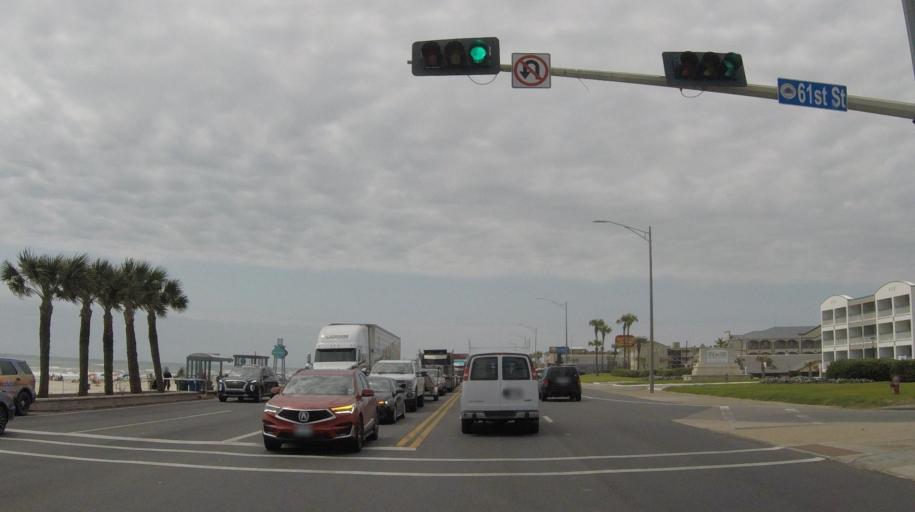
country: US
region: Texas
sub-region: Galveston County
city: Galveston
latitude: 29.2665
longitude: -94.8263
